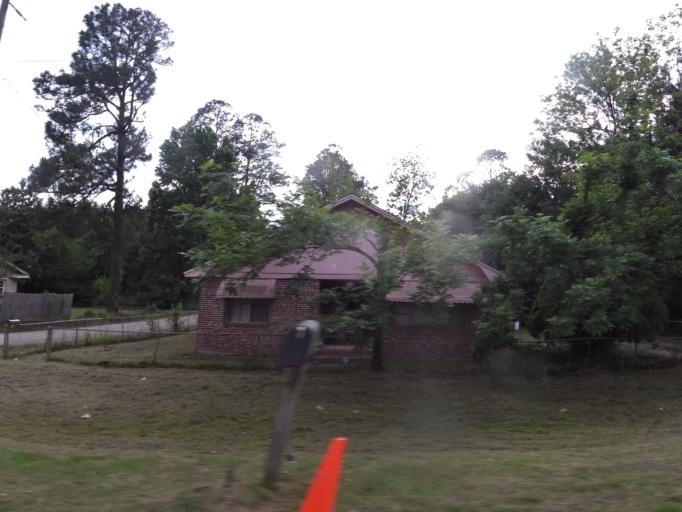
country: US
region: South Carolina
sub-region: Jasper County
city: Hardeeville
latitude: 32.2974
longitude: -81.0863
